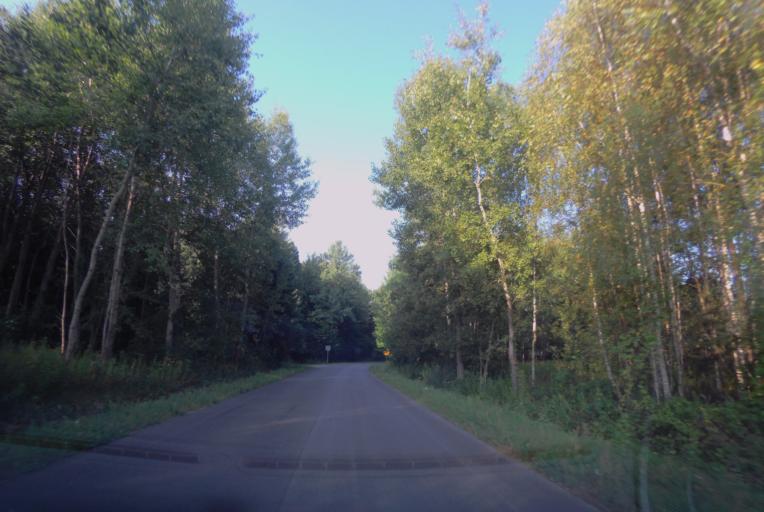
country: PL
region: Subcarpathian Voivodeship
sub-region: Powiat nizanski
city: Harasiuki
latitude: 50.5374
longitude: 22.5161
